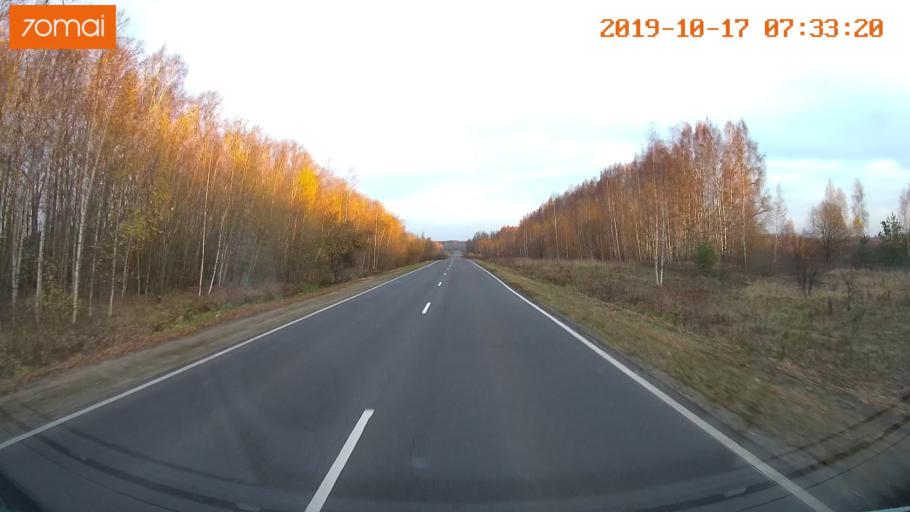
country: RU
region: Ivanovo
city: Gavrilov Posad
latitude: 56.4058
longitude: 39.9589
